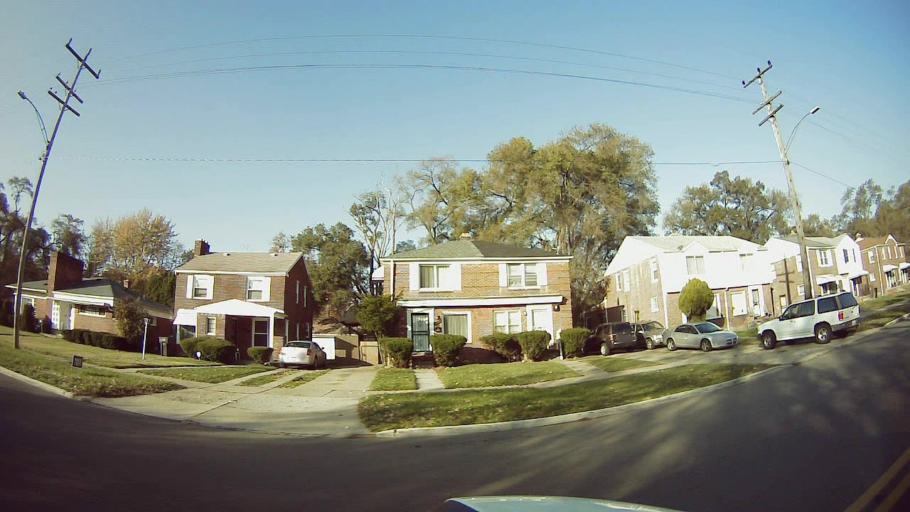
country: US
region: Michigan
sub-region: Oakland County
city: Oak Park
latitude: 42.4226
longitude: -83.1703
